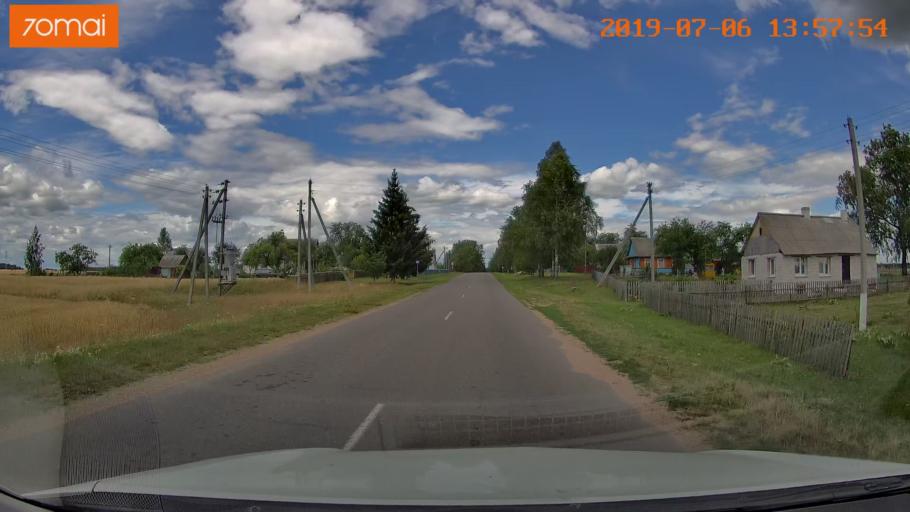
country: BY
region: Minsk
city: Ivyanyets
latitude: 53.7785
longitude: 26.8074
